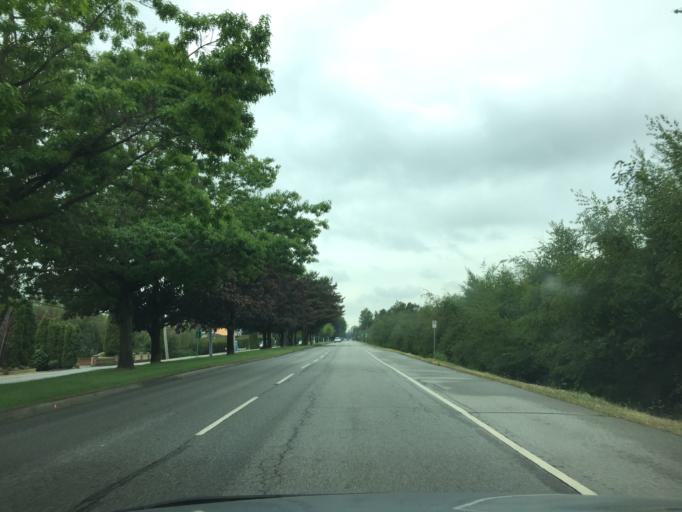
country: CA
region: British Columbia
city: Richmond
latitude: 49.1702
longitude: -123.1041
